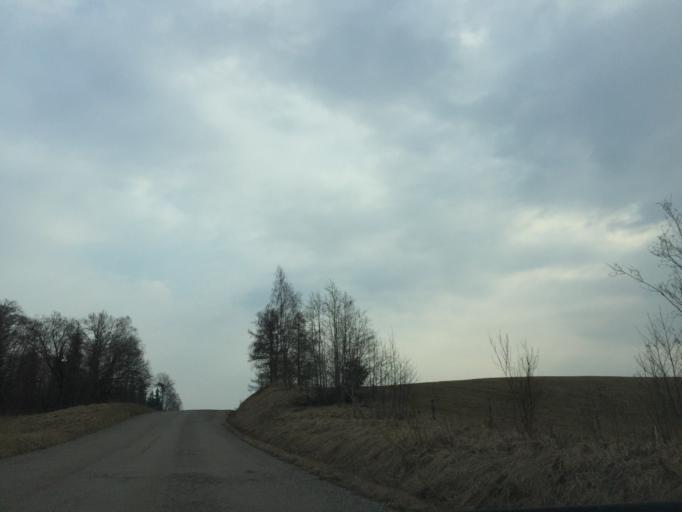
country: LV
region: Priekuli
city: Priekuli
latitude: 57.2496
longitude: 25.3717
